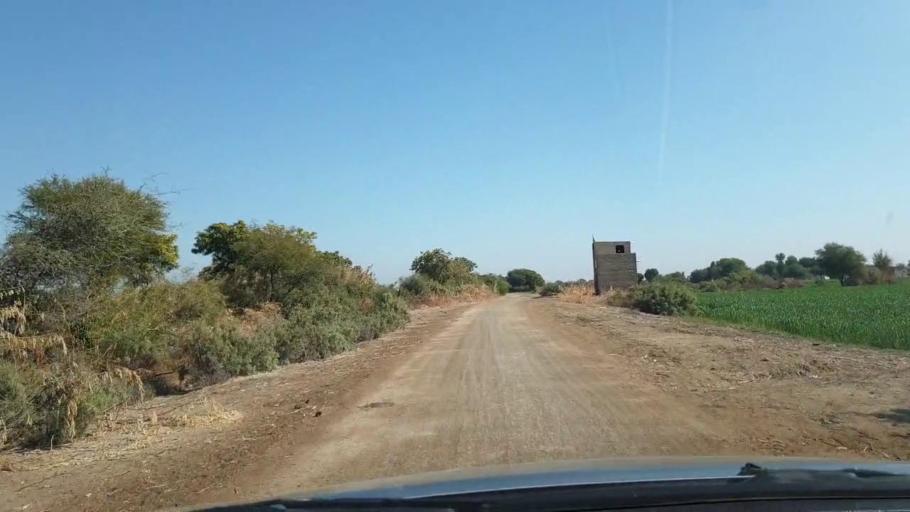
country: PK
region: Sindh
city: Jhol
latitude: 25.9226
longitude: 68.9451
